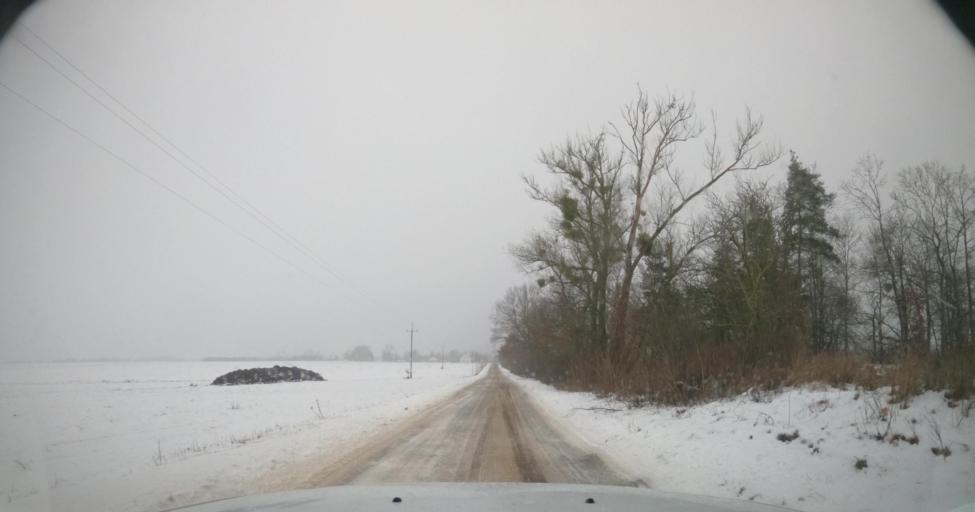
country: PL
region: West Pomeranian Voivodeship
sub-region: Powiat kamienski
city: Golczewo
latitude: 53.8050
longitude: 14.9666
